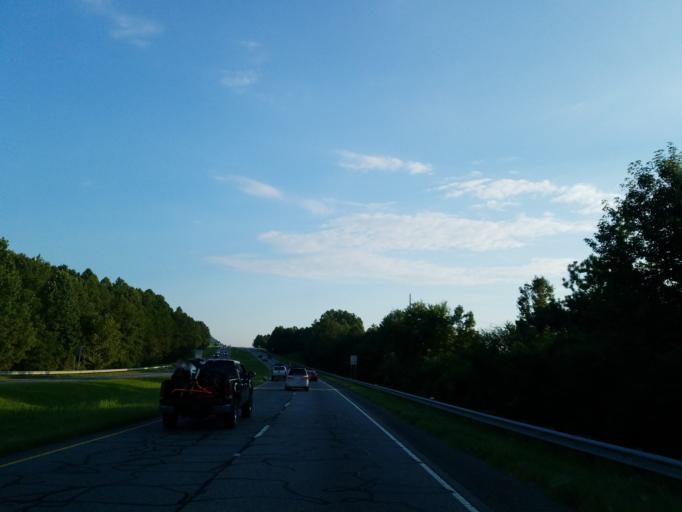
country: US
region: Georgia
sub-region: Gilmer County
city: Ellijay
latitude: 34.6523
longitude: -84.4957
